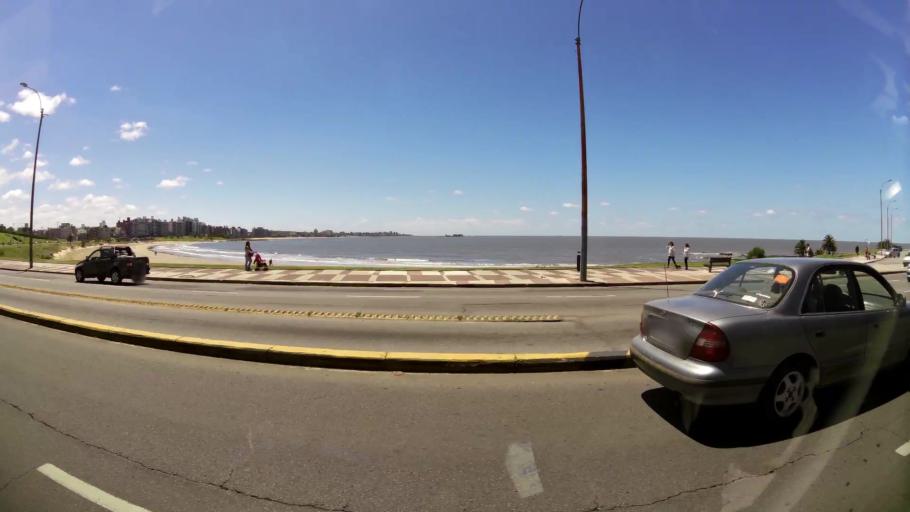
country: UY
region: Montevideo
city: Montevideo
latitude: -34.9019
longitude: -56.1241
